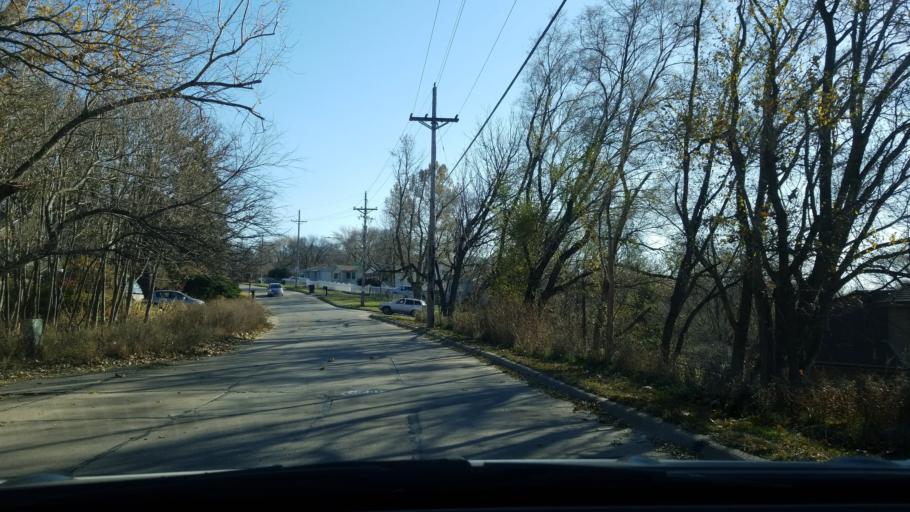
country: US
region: Nebraska
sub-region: Sarpy County
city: Bellevue
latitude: 41.1554
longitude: -95.9010
